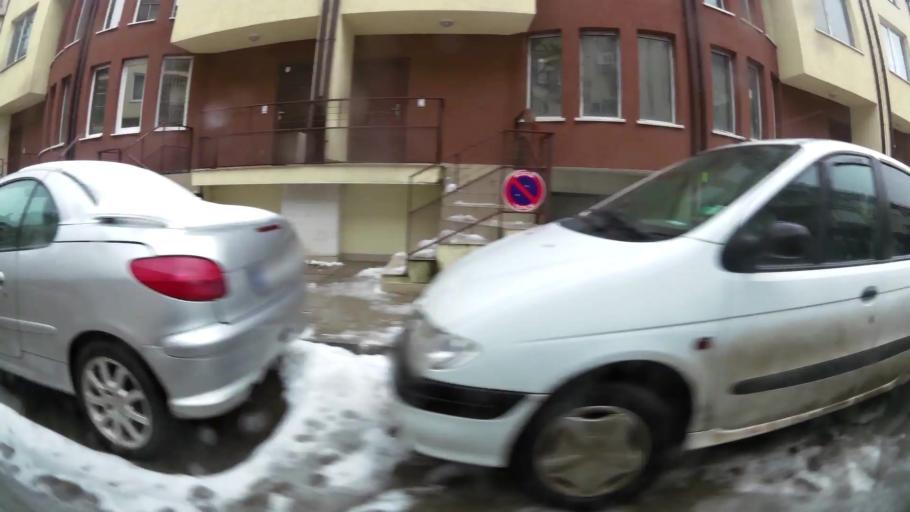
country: BG
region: Sofia-Capital
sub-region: Stolichna Obshtina
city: Sofia
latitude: 42.6618
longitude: 23.2917
